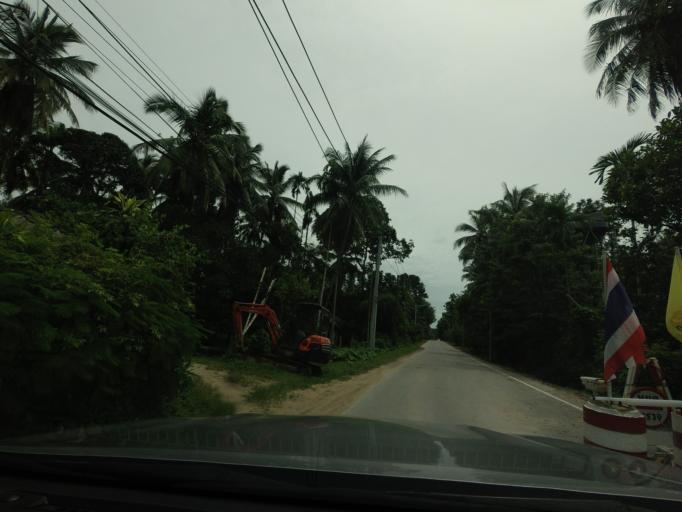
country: TH
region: Pattani
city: Kapho
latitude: 6.5661
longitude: 101.5338
